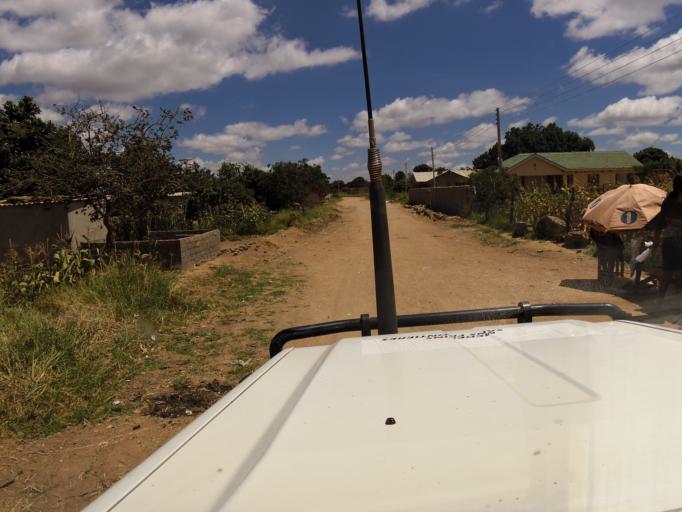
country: ZW
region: Harare
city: Epworth
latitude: -17.9024
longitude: 31.1613
